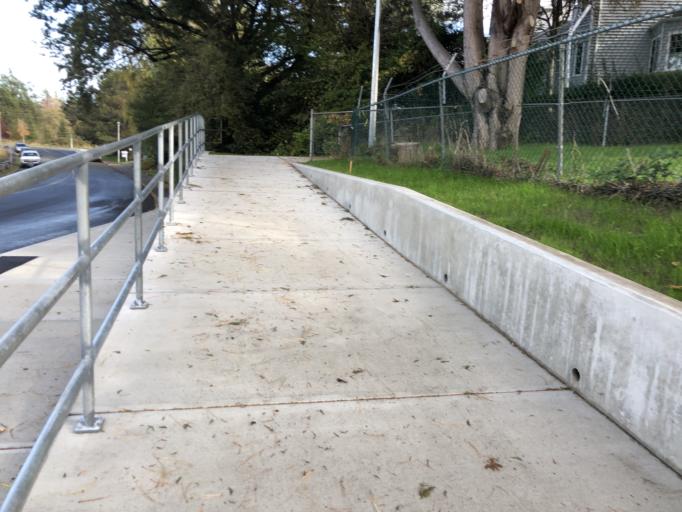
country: CA
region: British Columbia
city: Victoria
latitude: 48.4650
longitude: -123.3920
